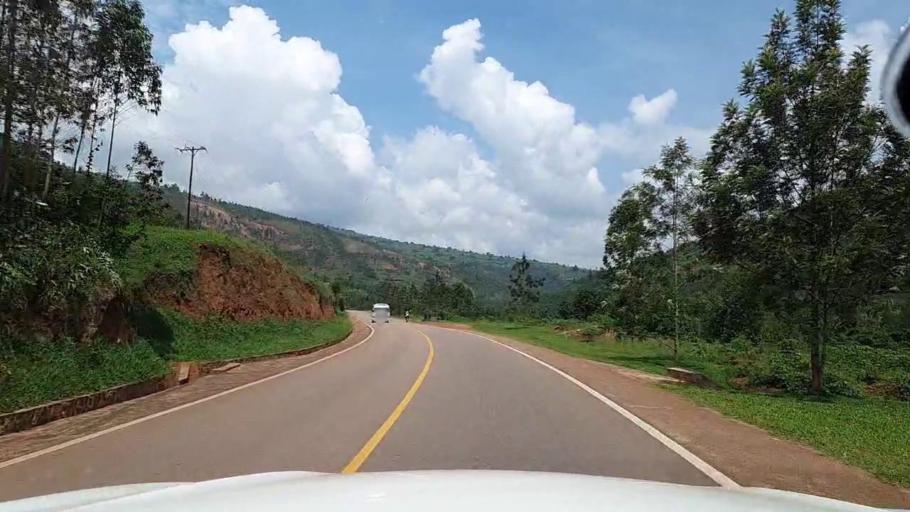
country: RW
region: Kigali
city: Kigali
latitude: -1.8401
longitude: 30.0843
